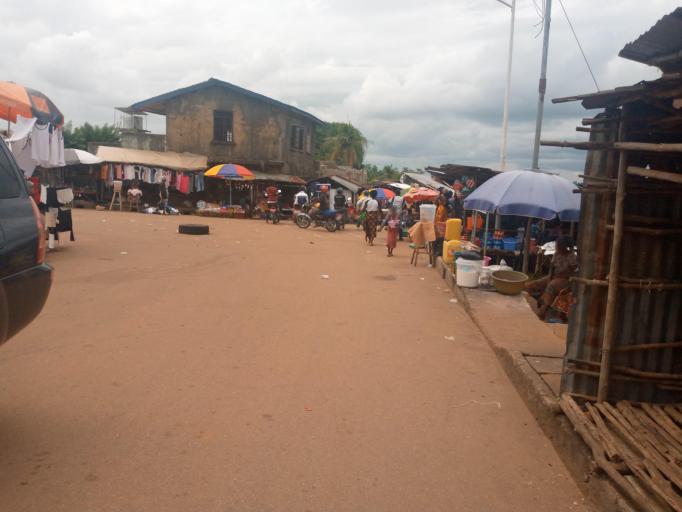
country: SL
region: Southern Province
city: Mogbwemo
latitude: 7.6054
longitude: -12.1801
